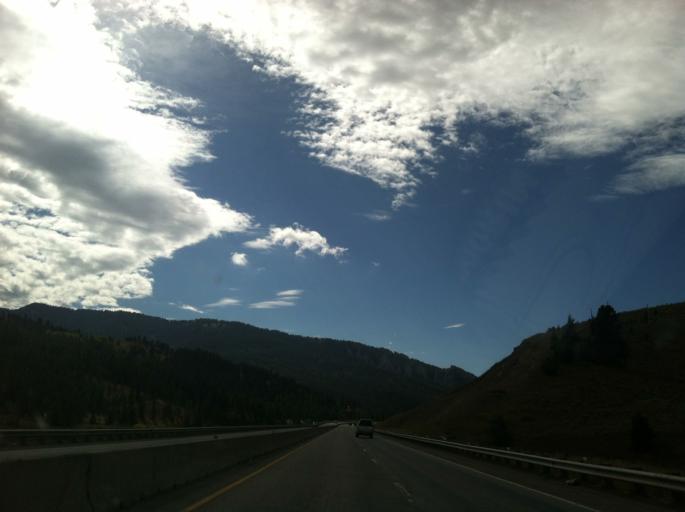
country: US
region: Montana
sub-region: Gallatin County
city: Bozeman
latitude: 45.6504
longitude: -110.8596
